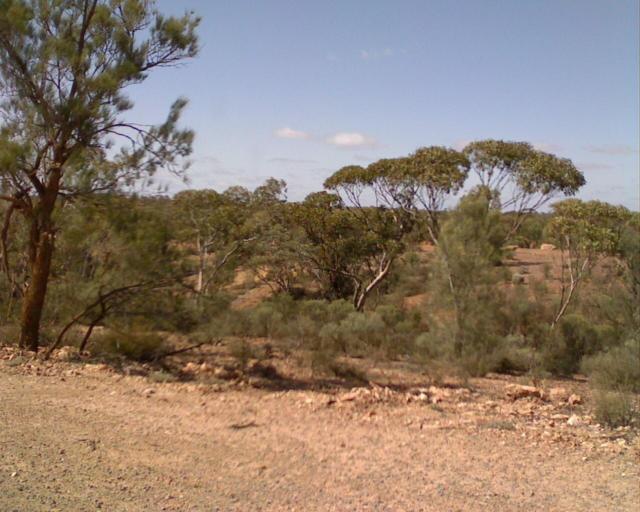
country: AU
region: Western Australia
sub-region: Kalgoorlie/Boulder
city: Boulder
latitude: -30.8437
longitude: 121.3906
